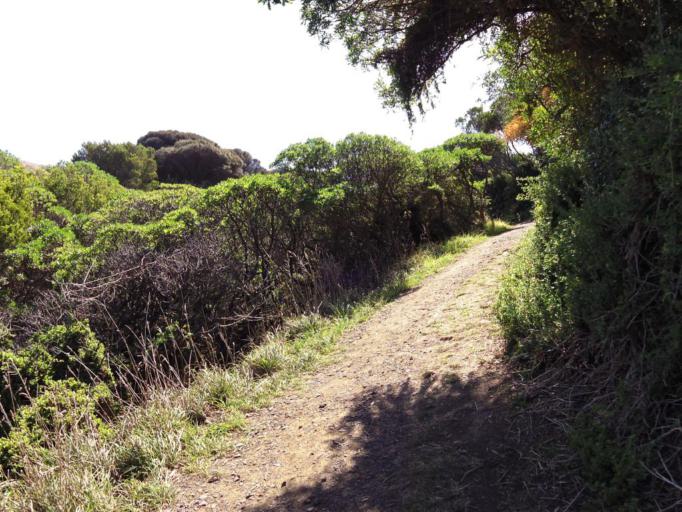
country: AU
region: Victoria
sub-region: Bass Coast
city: North Wonthaggi
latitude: -38.5364
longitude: 145.4253
